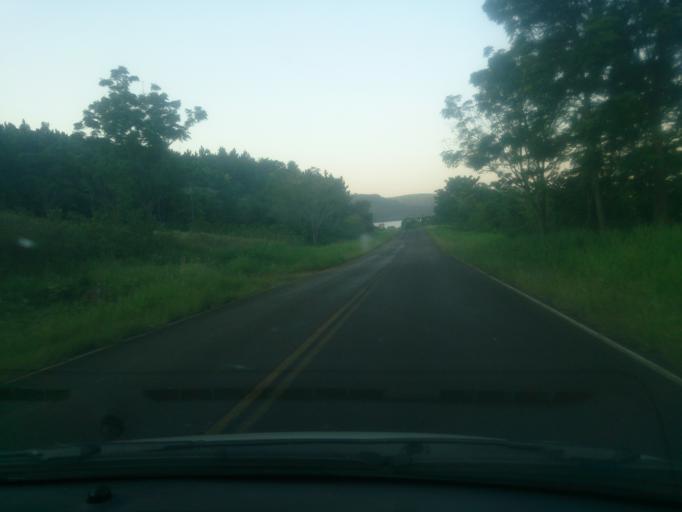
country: AR
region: Misiones
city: Panambi
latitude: -27.6582
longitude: -54.9088
